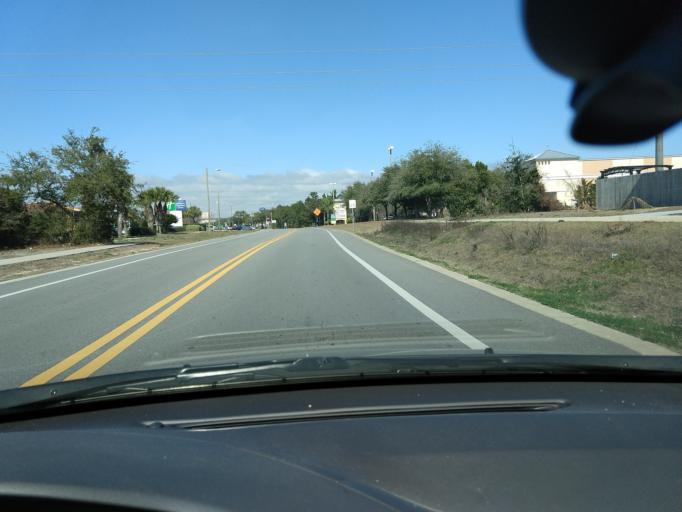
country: US
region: Florida
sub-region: Walton County
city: Miramar Beach
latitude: 30.3862
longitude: -86.4259
